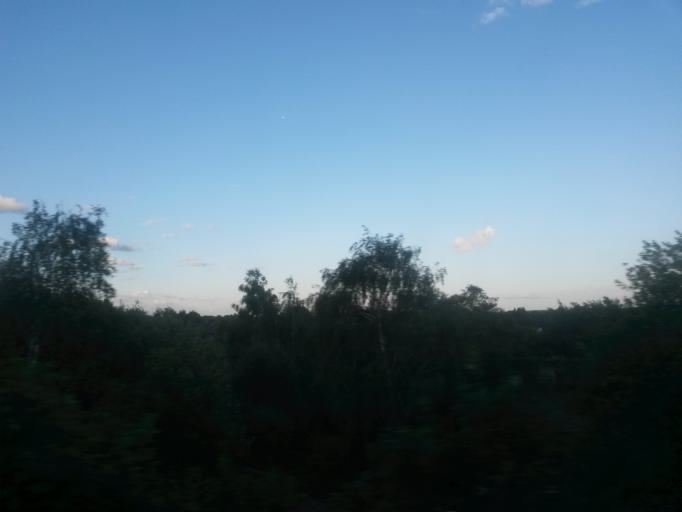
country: GB
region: England
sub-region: Greater London
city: Croydon
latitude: 51.3874
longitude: -0.0858
